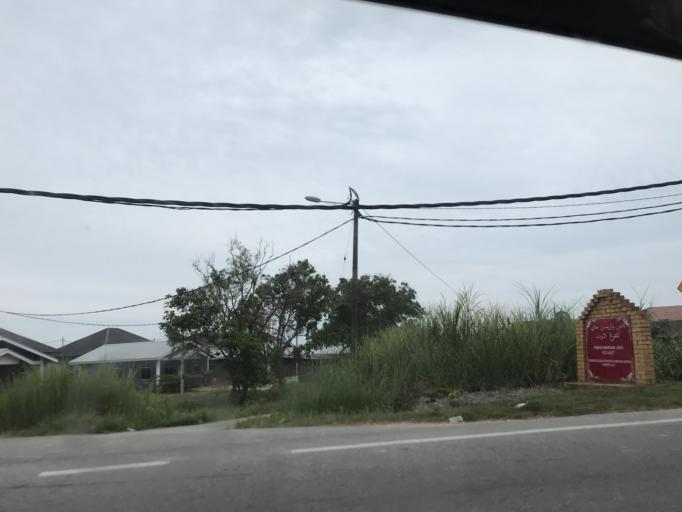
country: MY
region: Kelantan
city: Kota Bharu
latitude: 6.1534
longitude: 102.2267
